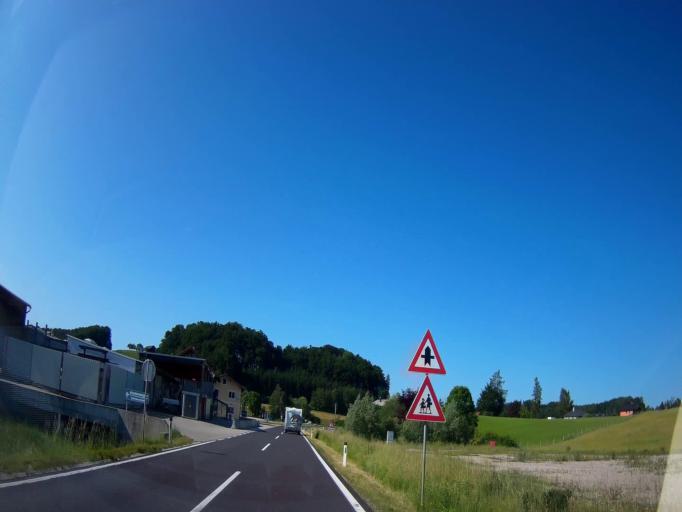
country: AT
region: Salzburg
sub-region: Politischer Bezirk Salzburg-Umgebung
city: Dorfbeuern
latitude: 48.1239
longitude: 13.0077
